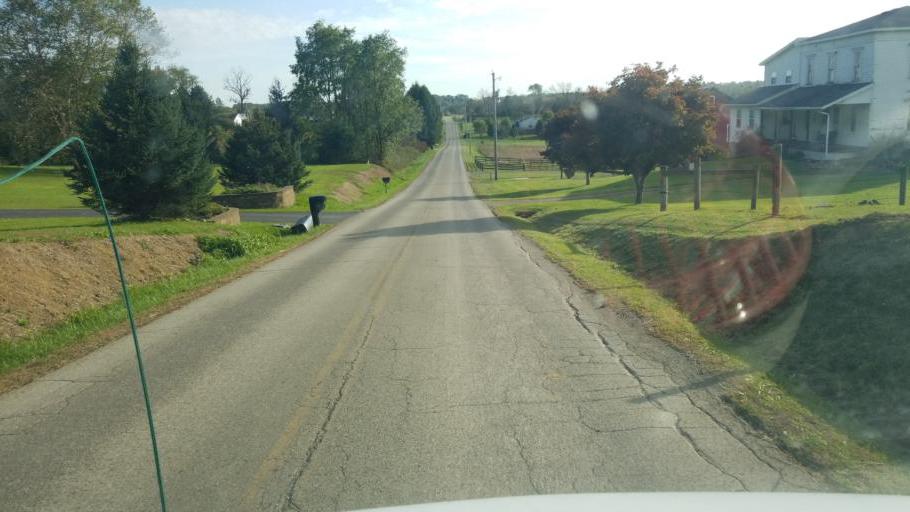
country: US
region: Ohio
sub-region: Wayne County
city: Shreve
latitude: 40.6523
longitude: -82.0818
